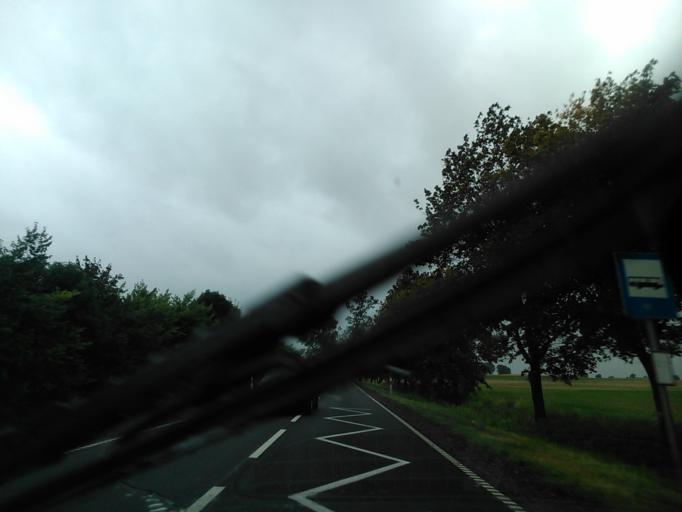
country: PL
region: Kujawsko-Pomorskie
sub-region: Powiat mogilenski
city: Strzelno
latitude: 52.6290
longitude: 18.1362
